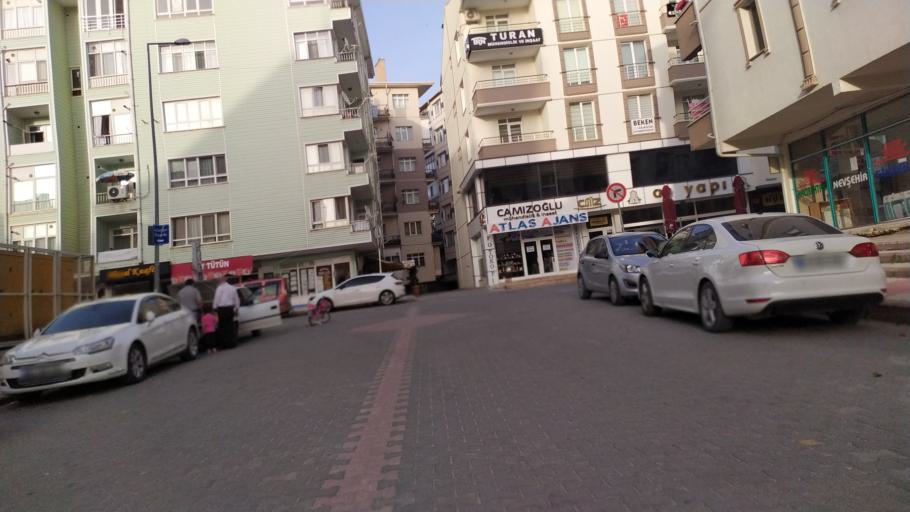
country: TR
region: Kirsehir
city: Kirsehir
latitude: 39.1459
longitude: 34.1640
